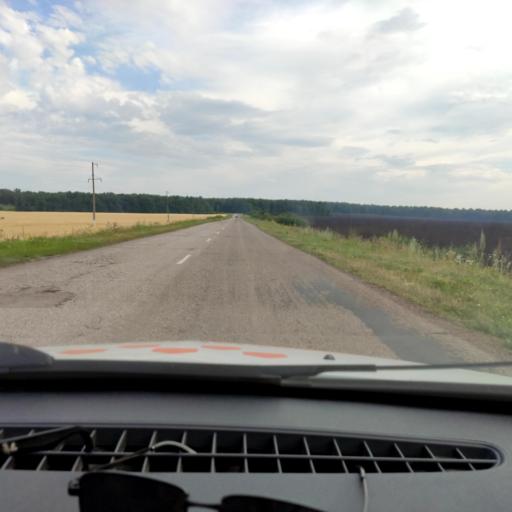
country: RU
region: Bashkortostan
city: Chishmy
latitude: 54.4671
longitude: 55.5412
